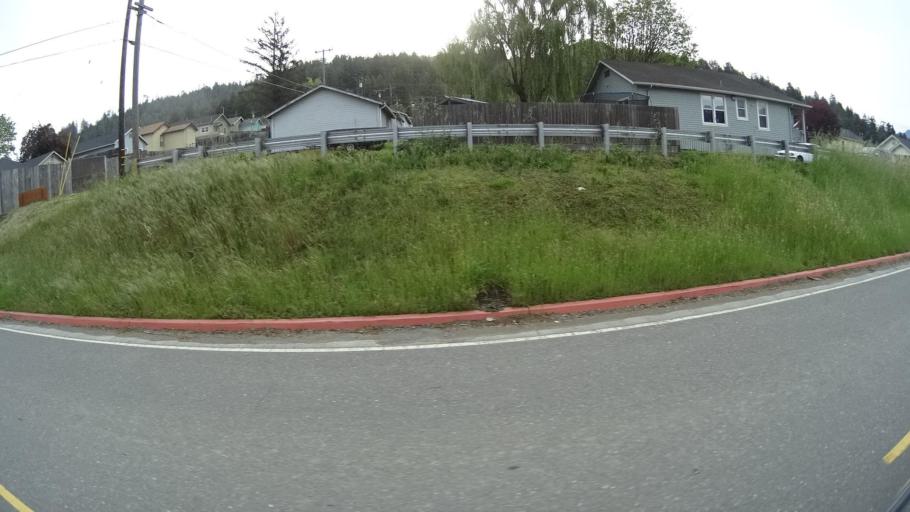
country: US
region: California
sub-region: Humboldt County
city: Rio Dell
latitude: 40.4796
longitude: -124.1029
